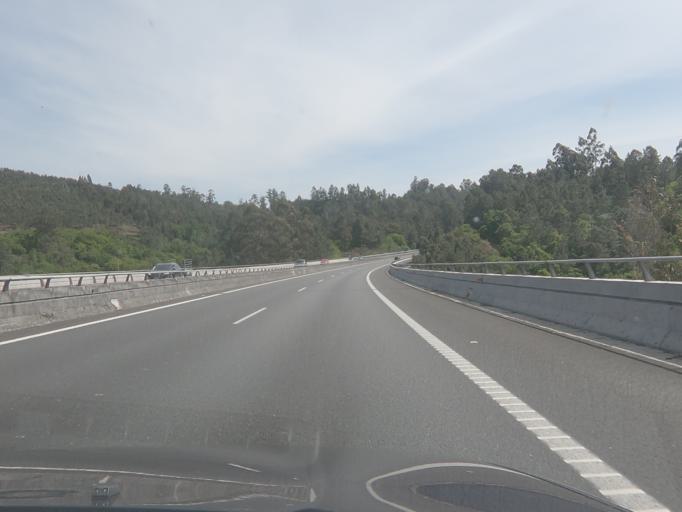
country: ES
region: Galicia
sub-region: Provincia de Pontevedra
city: Valga
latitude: 42.6781
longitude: -8.6335
